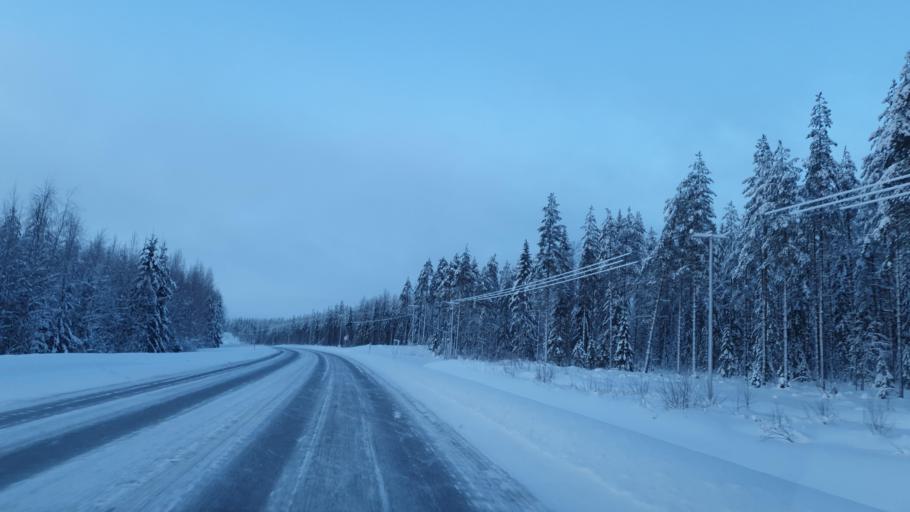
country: FI
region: Kainuu
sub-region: Kajaani
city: Kajaani
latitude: 64.4418
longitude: 27.5512
